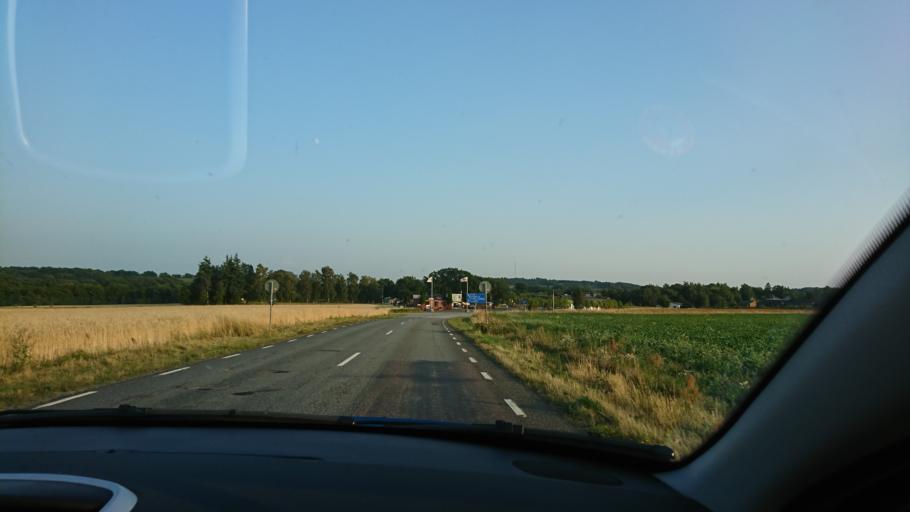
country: SE
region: Skane
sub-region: Simrishamns Kommun
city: Kivik
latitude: 55.6923
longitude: 14.1576
